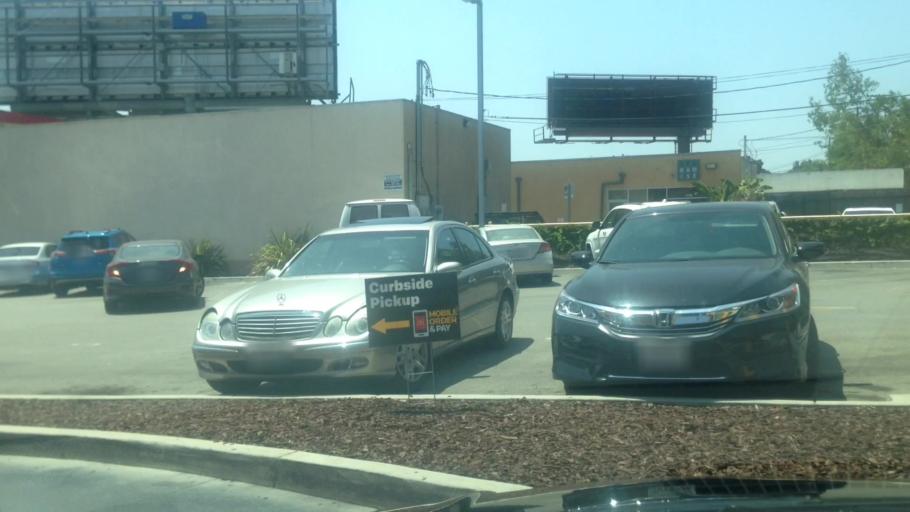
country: US
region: California
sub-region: Los Angeles County
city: West Hollywood
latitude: 34.0526
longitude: -118.3445
